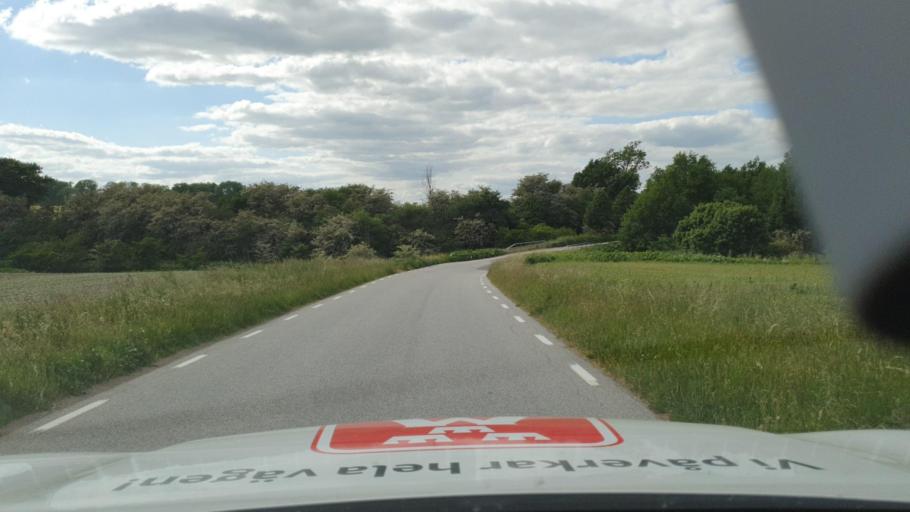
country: SE
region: Skane
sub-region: Ystads Kommun
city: Kopingebro
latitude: 55.4714
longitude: 14.0011
